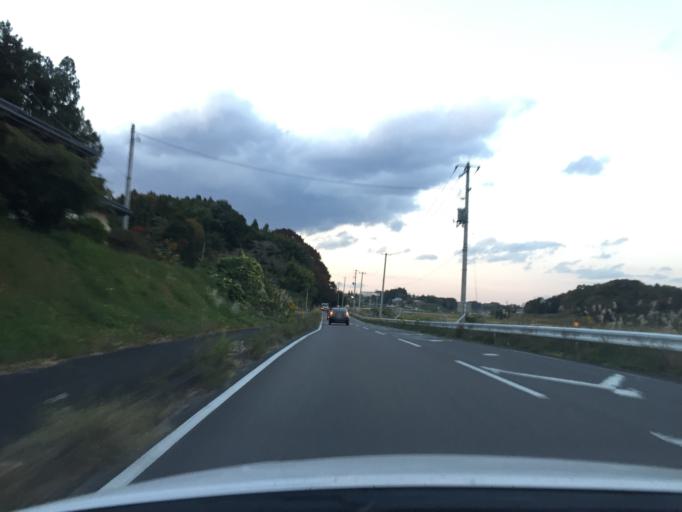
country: JP
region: Fukushima
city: Miharu
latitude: 37.4849
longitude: 140.4533
